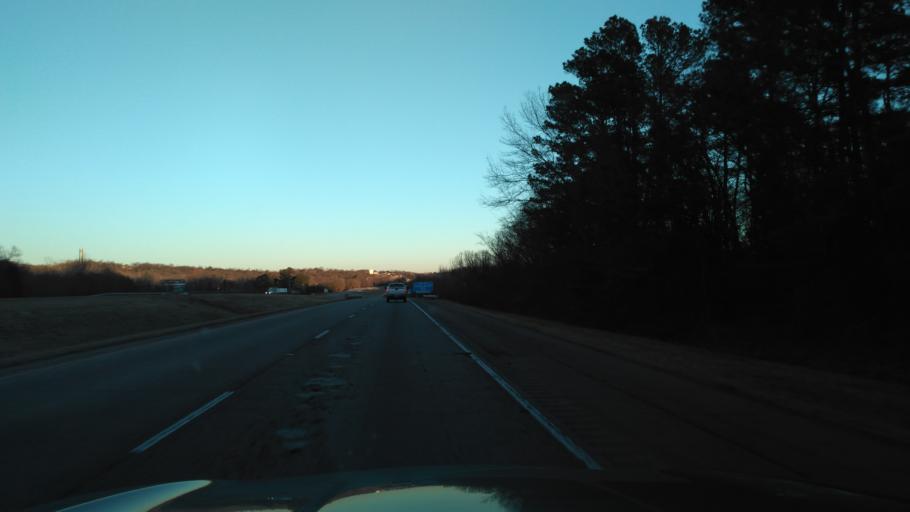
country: US
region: Arkansas
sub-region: Crawford County
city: Van Buren
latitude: 35.4621
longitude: -94.4202
